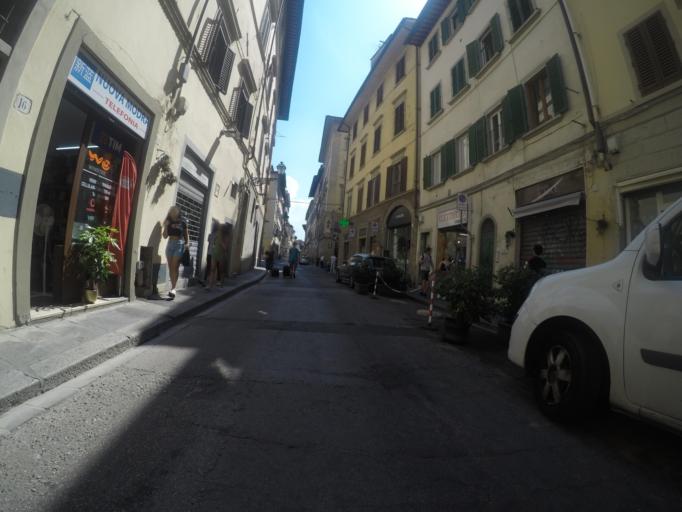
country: IT
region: Tuscany
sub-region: Province of Florence
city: Florence
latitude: 43.7773
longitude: 11.2557
